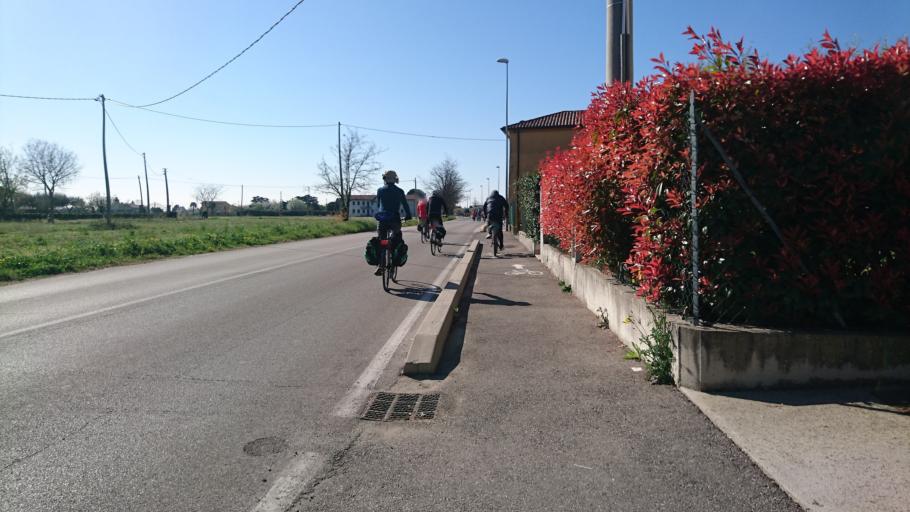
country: IT
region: Veneto
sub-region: Provincia di Vicenza
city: Bassano del Grappa
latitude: 45.7428
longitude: 11.7390
